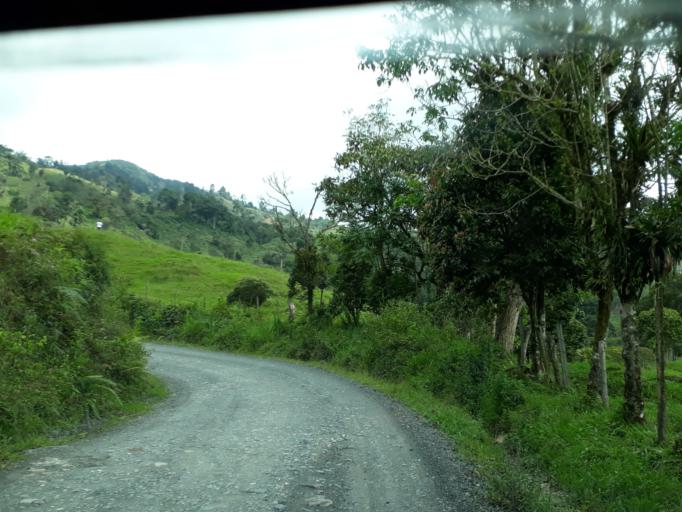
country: CO
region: Cundinamarca
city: Pacho
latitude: 5.2579
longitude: -74.1858
